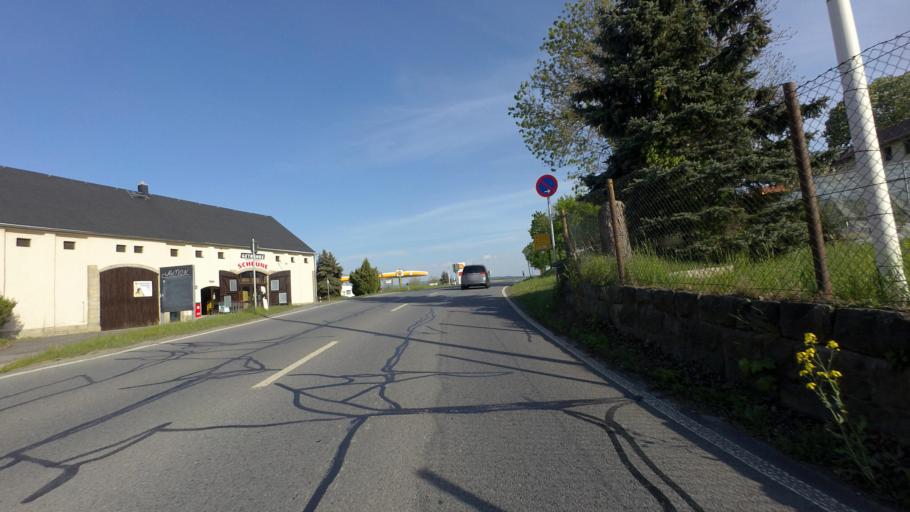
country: DE
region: Saxony
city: Stolpen
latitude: 51.0514
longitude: 14.0865
